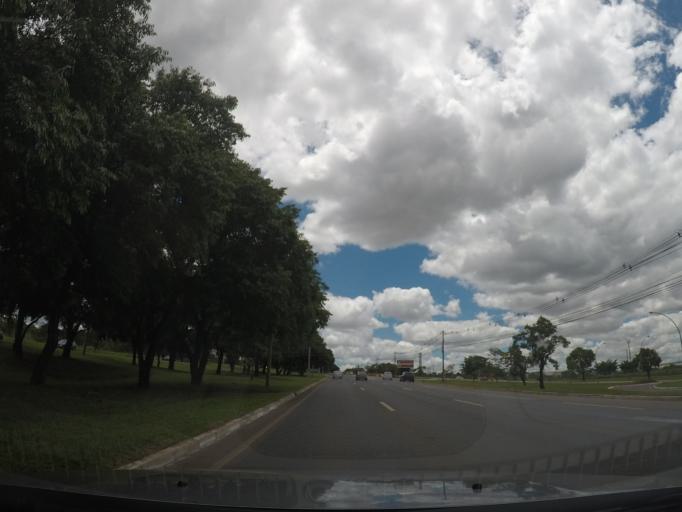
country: BR
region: Federal District
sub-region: Brasilia
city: Brasilia
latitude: -15.7519
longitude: -47.9245
